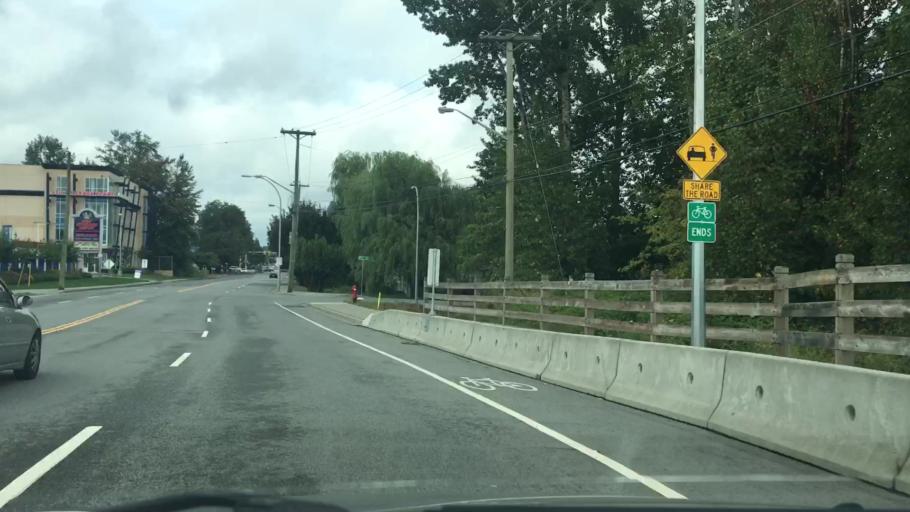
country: CA
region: British Columbia
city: Langley
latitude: 49.1047
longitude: -122.6380
